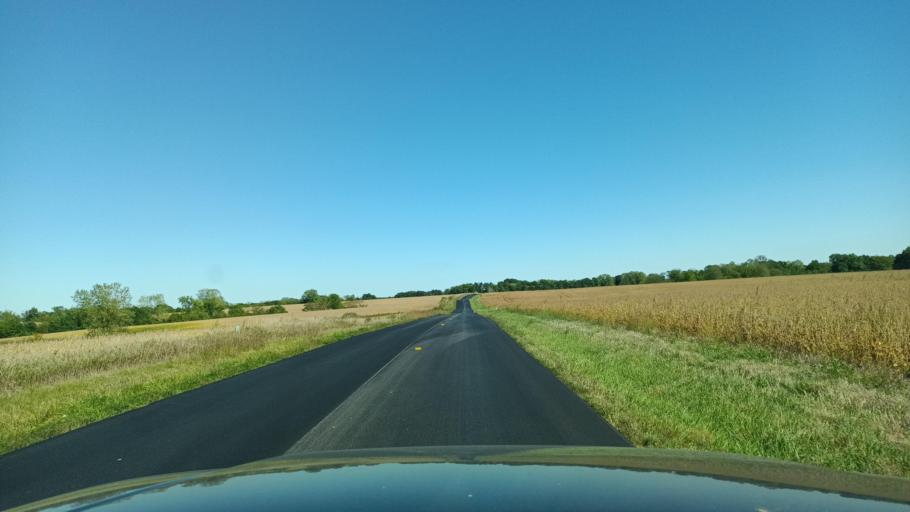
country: US
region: Missouri
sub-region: Macon County
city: La Plata
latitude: 39.9274
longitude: -92.5482
